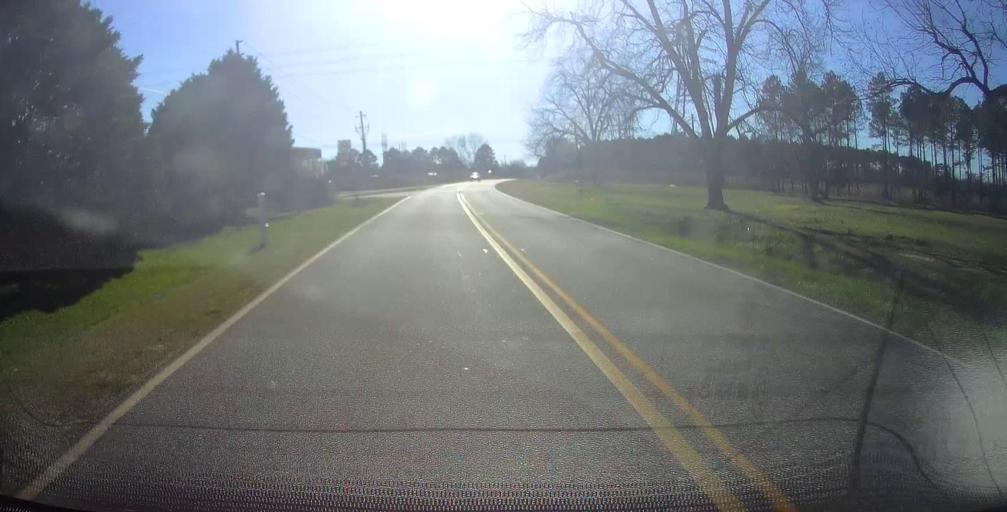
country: US
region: Georgia
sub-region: Sumter County
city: Americus
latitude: 32.0996
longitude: -84.2107
